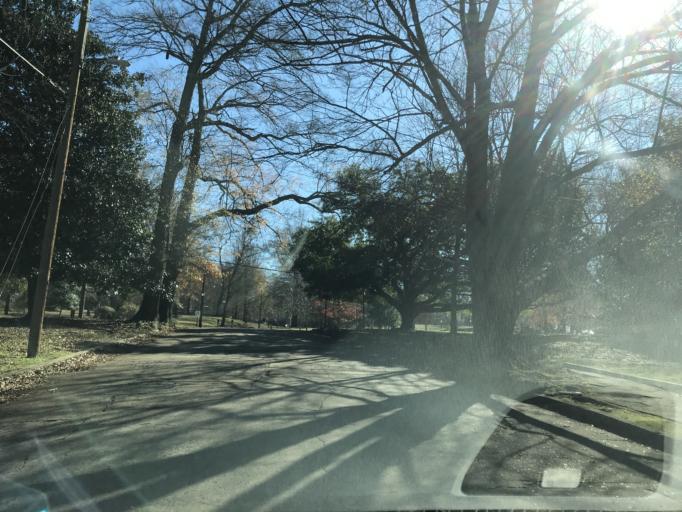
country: US
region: Georgia
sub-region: DeKalb County
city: Druid Hills
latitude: 33.7610
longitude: -84.3553
